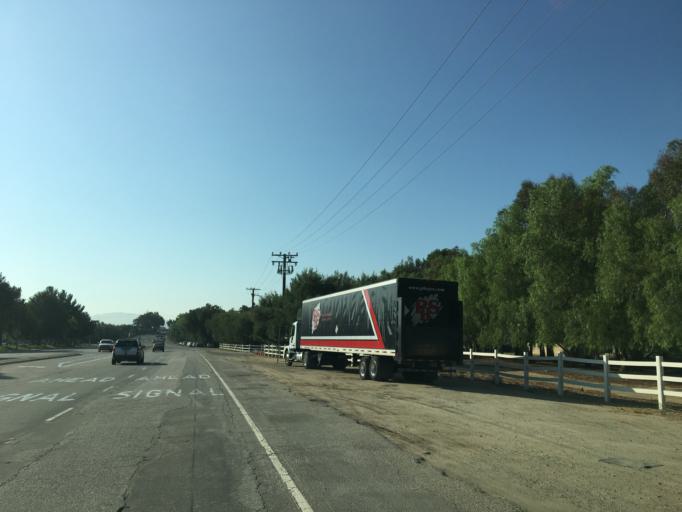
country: US
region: California
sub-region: Los Angeles County
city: Valencia
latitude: 34.4322
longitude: -118.5916
